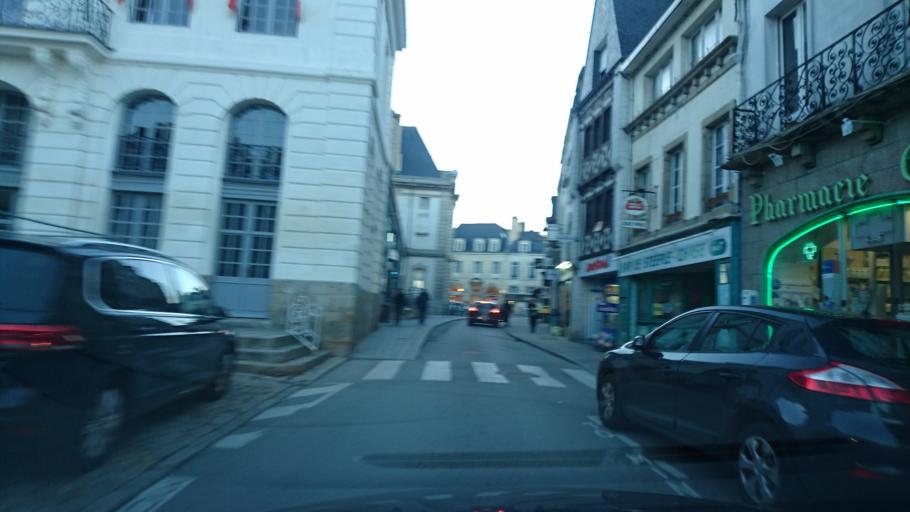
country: FR
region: Brittany
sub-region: Departement du Morbihan
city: Auray
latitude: 47.6665
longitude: -2.9833
